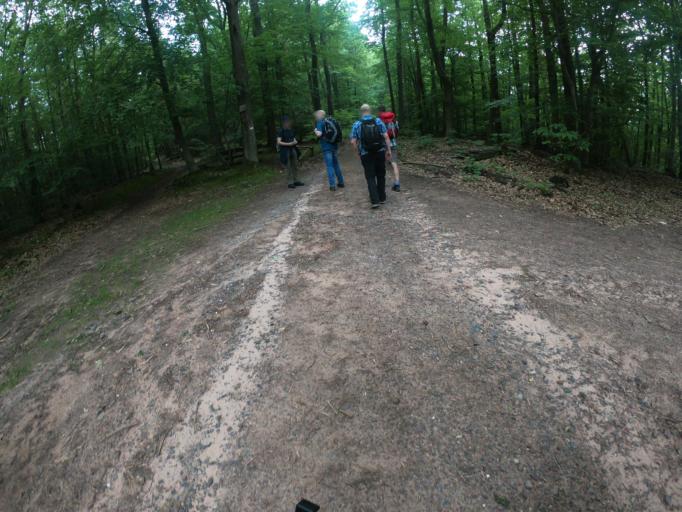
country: DE
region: Rheinland-Pfalz
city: Annweiler am Trifels
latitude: 49.1897
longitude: 7.9917
